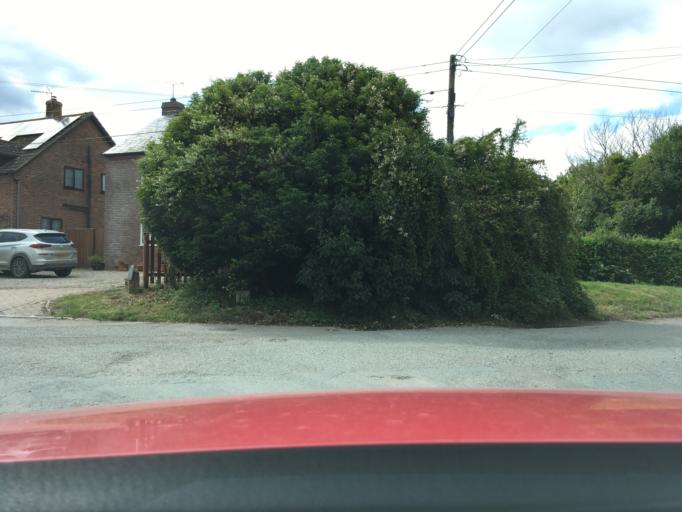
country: GB
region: England
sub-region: Gloucestershire
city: Cinderford
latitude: 51.8012
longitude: -2.4193
